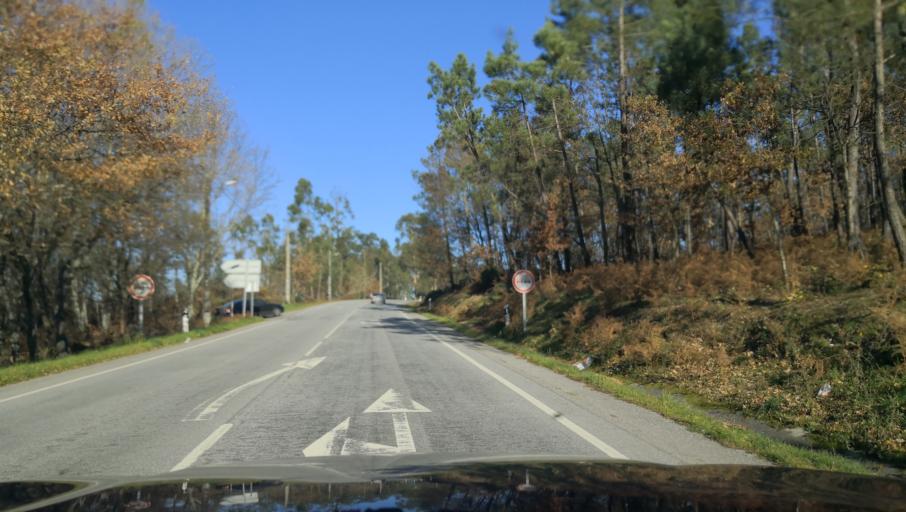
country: PT
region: Viseu
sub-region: Vouzela
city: Vouzela
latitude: 40.7124
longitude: -8.1393
